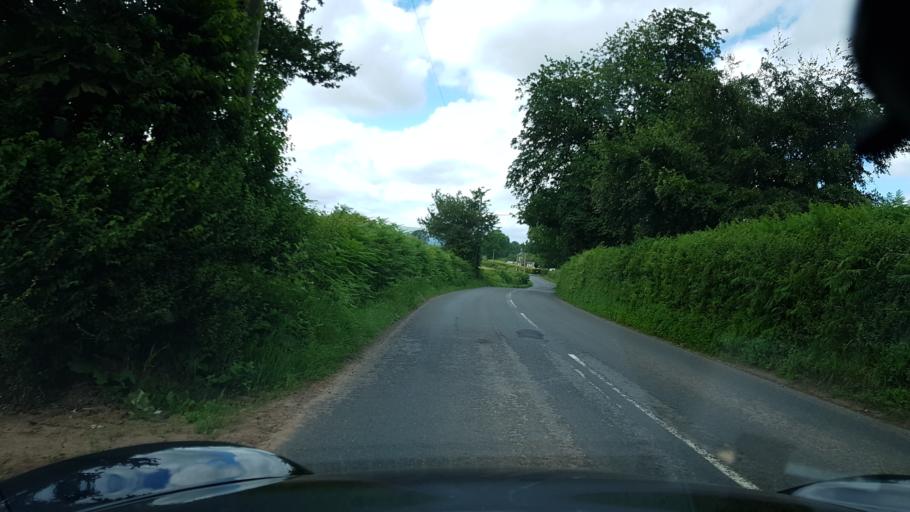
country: GB
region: Wales
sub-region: Monmouthshire
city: Usk
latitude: 51.7345
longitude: -2.9363
